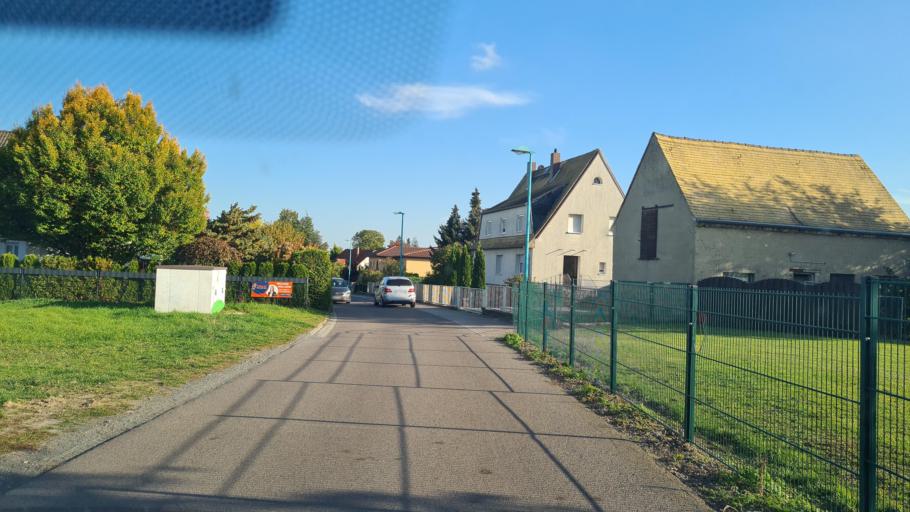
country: DE
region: Saxony
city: Machern
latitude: 51.3633
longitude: 12.6164
